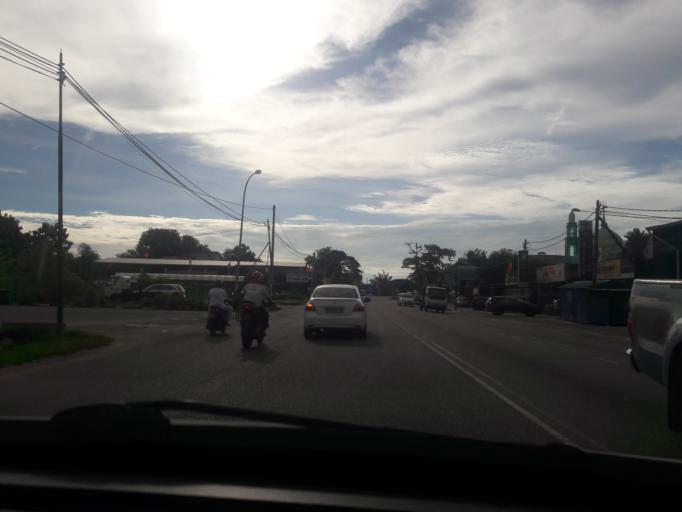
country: MY
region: Kedah
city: Sungai Petani
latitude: 5.6348
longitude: 100.5019
